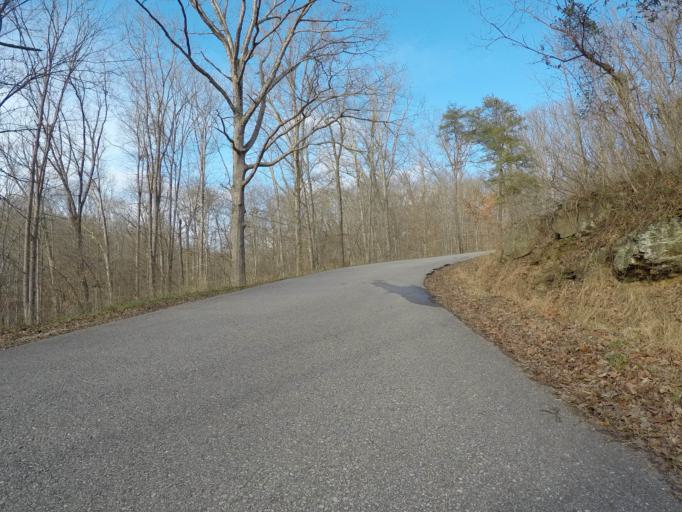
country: US
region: West Virginia
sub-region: Cabell County
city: Pea Ridge
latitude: 38.4300
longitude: -82.3391
